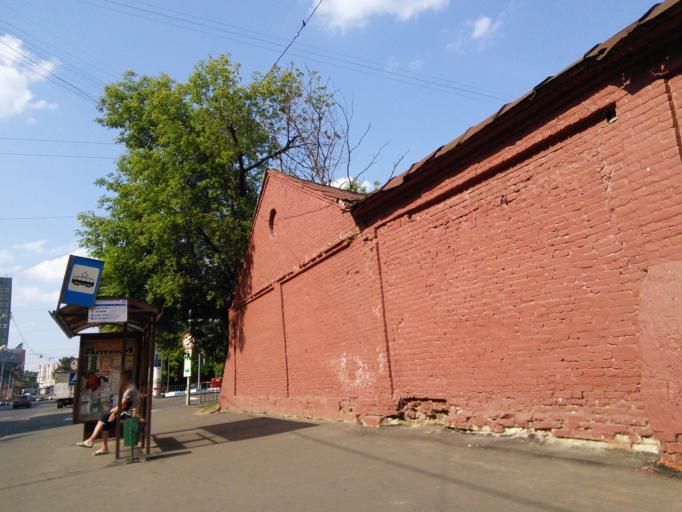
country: RU
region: Moskovskaya
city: Bogorodskoye
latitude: 55.7935
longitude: 37.7148
